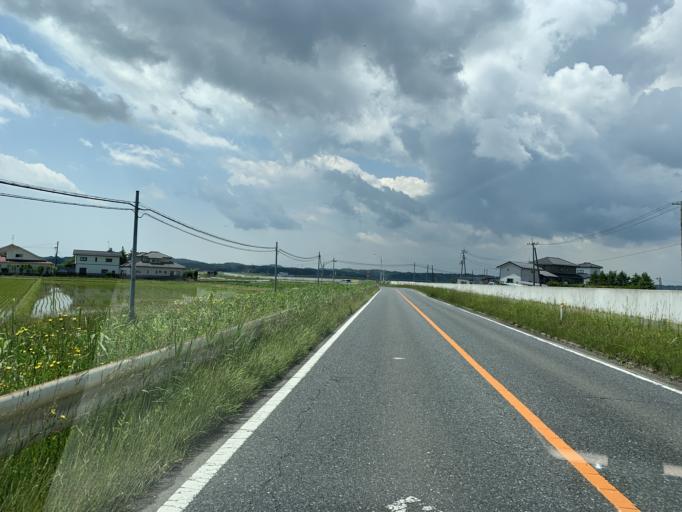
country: JP
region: Miyagi
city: Matsushima
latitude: 38.4509
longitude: 141.0820
